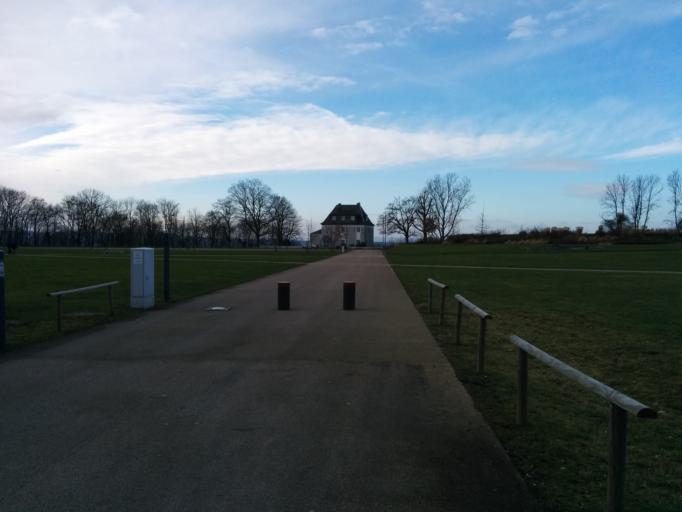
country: DE
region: Rheinland-Pfalz
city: Urbar
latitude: 50.3691
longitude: 7.6181
